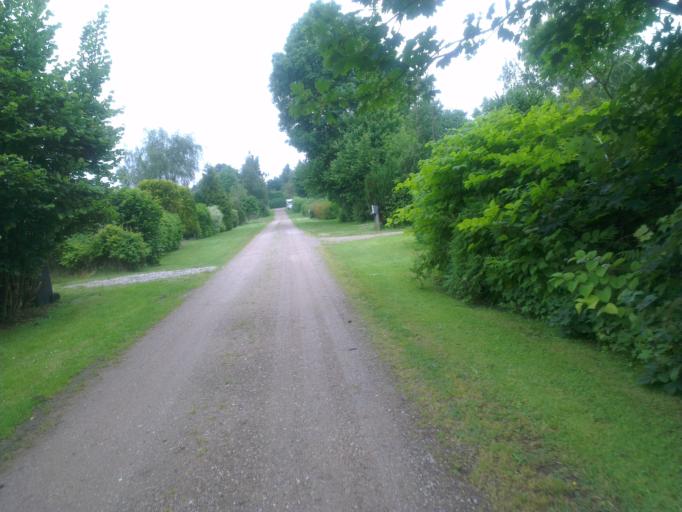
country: DK
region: Capital Region
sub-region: Frederikssund Kommune
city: Jaegerspris
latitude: 55.9043
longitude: 11.9376
